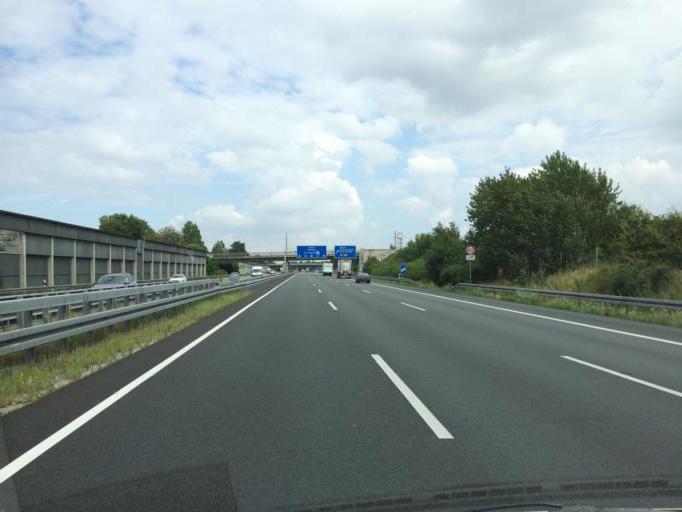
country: DE
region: Lower Saxony
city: Vordorf
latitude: 52.3175
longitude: 10.5042
